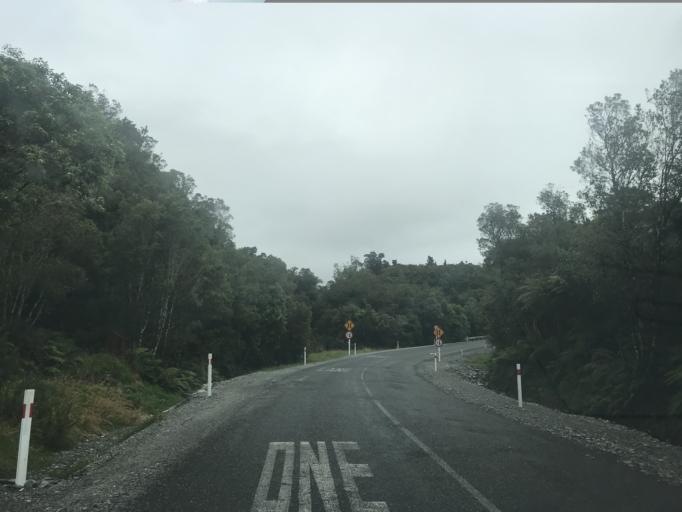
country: NZ
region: West Coast
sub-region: Westland District
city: Hokitika
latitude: -42.9544
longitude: 171.0226
